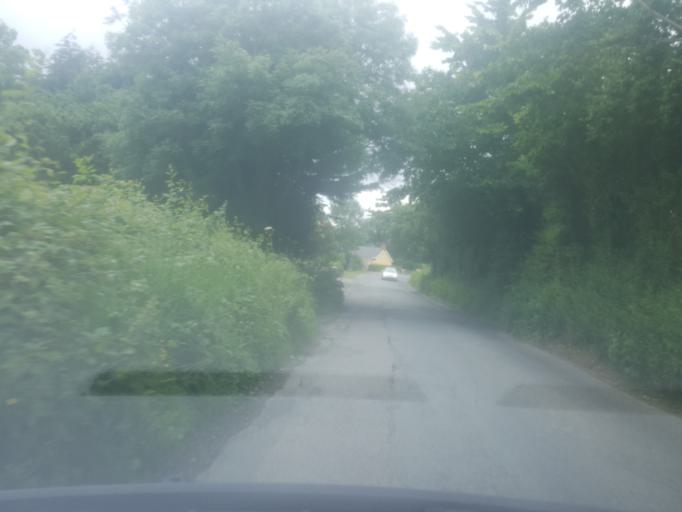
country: IE
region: Munster
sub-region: Ciarrai
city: Cill Airne
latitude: 52.0828
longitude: -9.4929
